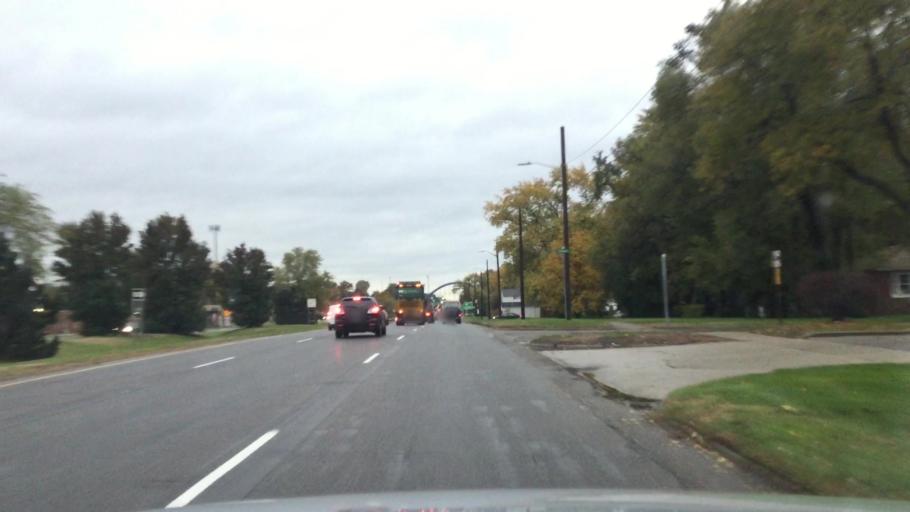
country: US
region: Michigan
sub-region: Wayne County
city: Taylor
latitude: 42.2741
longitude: -83.2708
